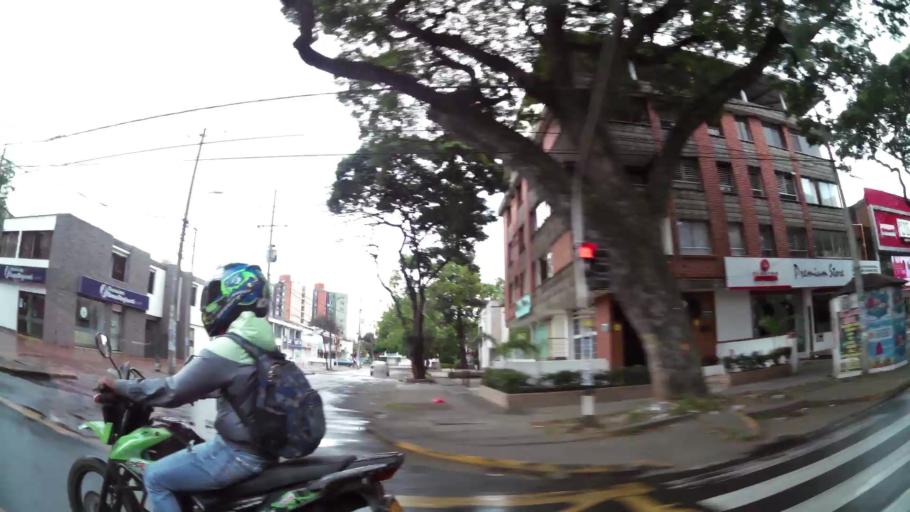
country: CO
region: Valle del Cauca
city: Cali
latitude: 3.4713
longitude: -76.5271
